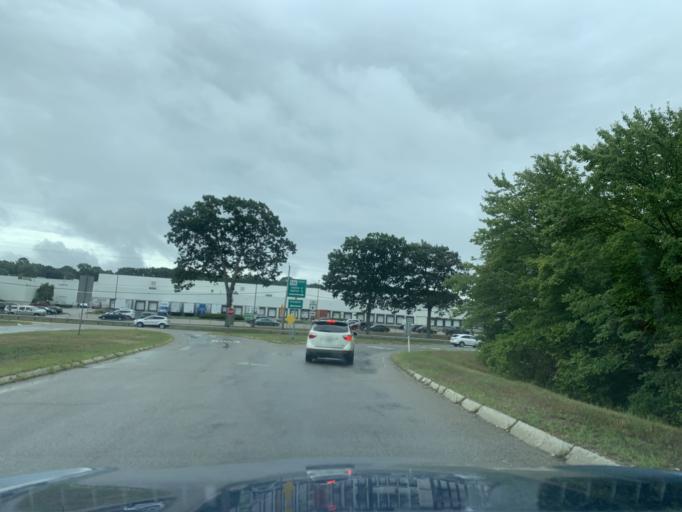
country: US
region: Rhode Island
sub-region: Bristol County
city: Warren
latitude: 41.7725
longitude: -71.2636
